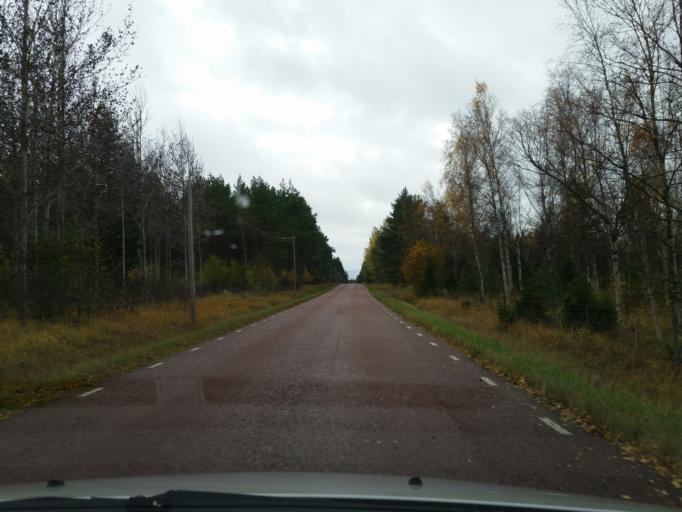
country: AX
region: Alands landsbygd
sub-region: Lemland
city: Lemland
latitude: 60.0077
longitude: 20.1870
